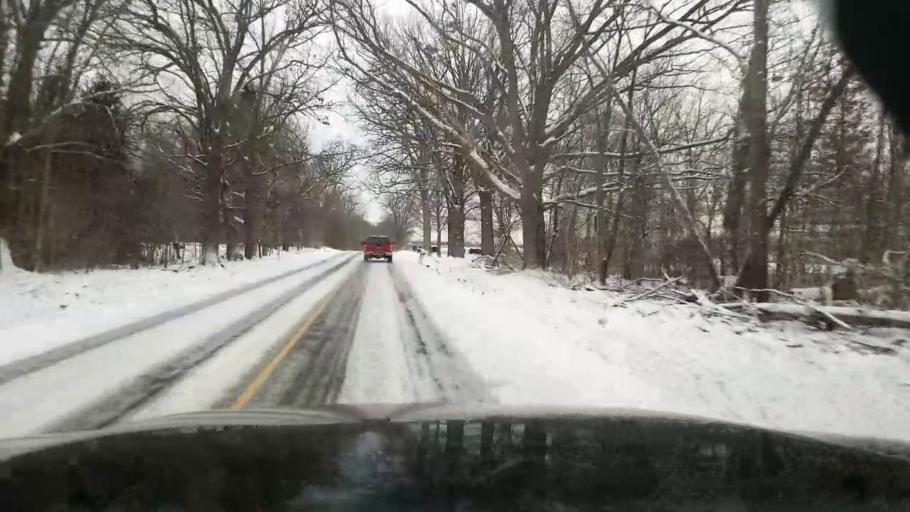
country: US
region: Michigan
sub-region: Jackson County
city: Spring Arbor
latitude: 42.1758
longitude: -84.5006
